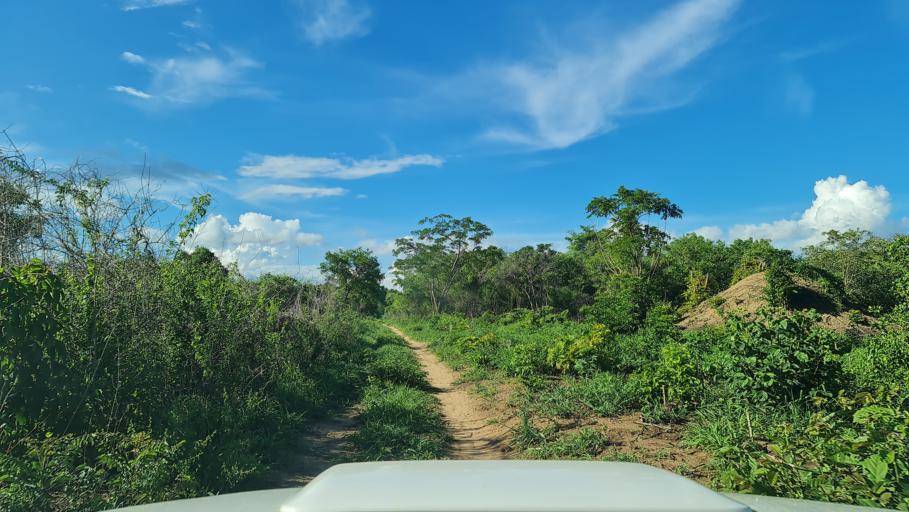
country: MZ
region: Nampula
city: Ilha de Mocambique
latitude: -15.2643
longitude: 40.1858
